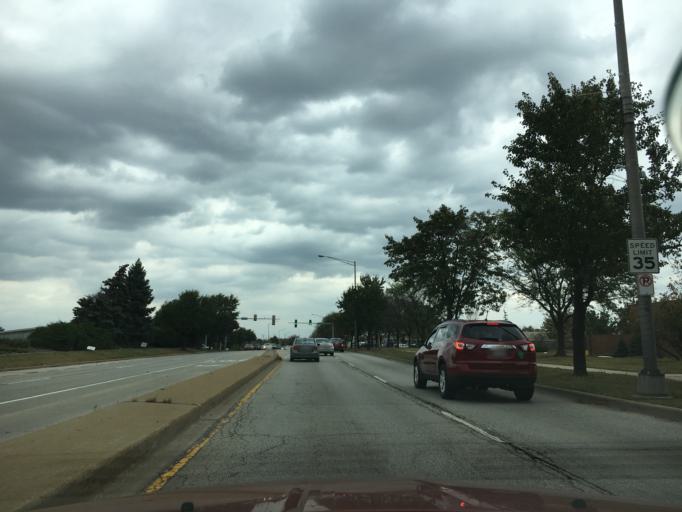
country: US
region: Illinois
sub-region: Cook County
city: Orland Hills
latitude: 41.6031
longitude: -87.8479
